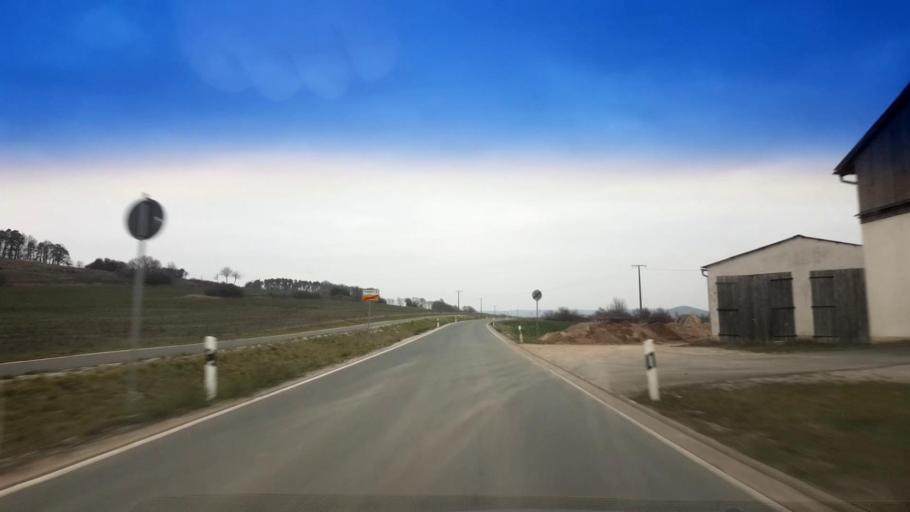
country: DE
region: Bavaria
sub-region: Upper Franconia
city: Hallerndorf
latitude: 49.7641
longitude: 10.9870
